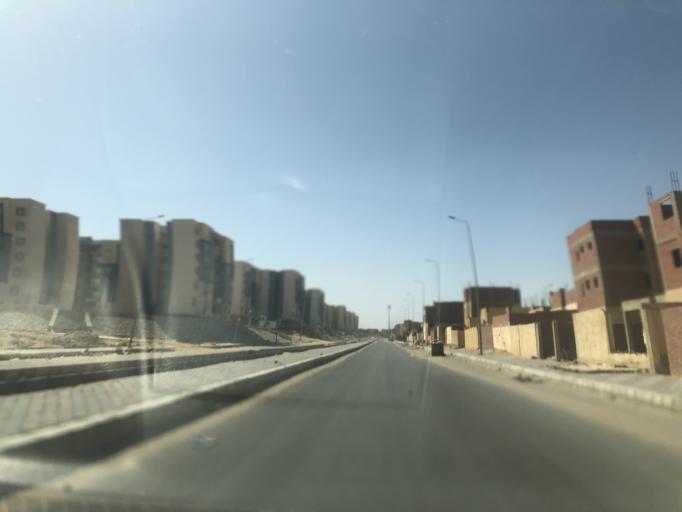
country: EG
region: Al Jizah
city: Madinat Sittah Uktubar
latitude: 29.9321
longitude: 30.9852
